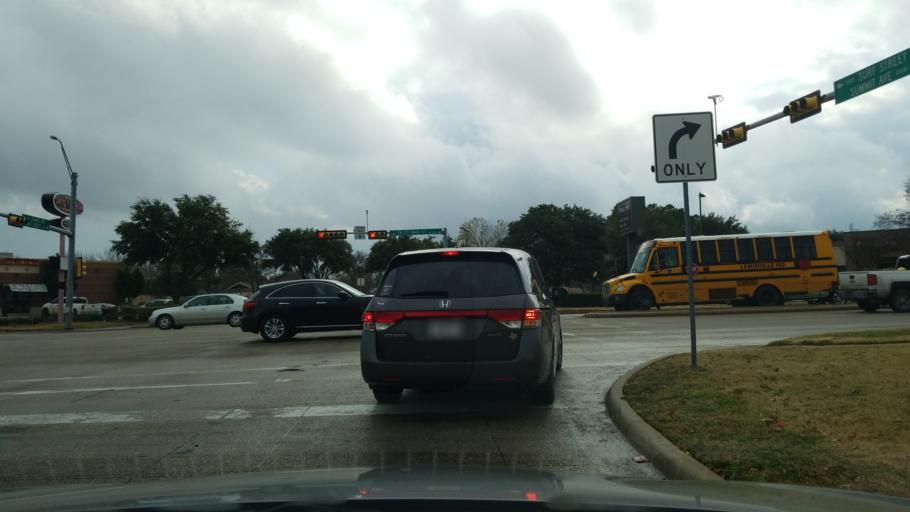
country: US
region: Texas
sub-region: Denton County
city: Lewisville
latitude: 33.0447
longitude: -97.0144
